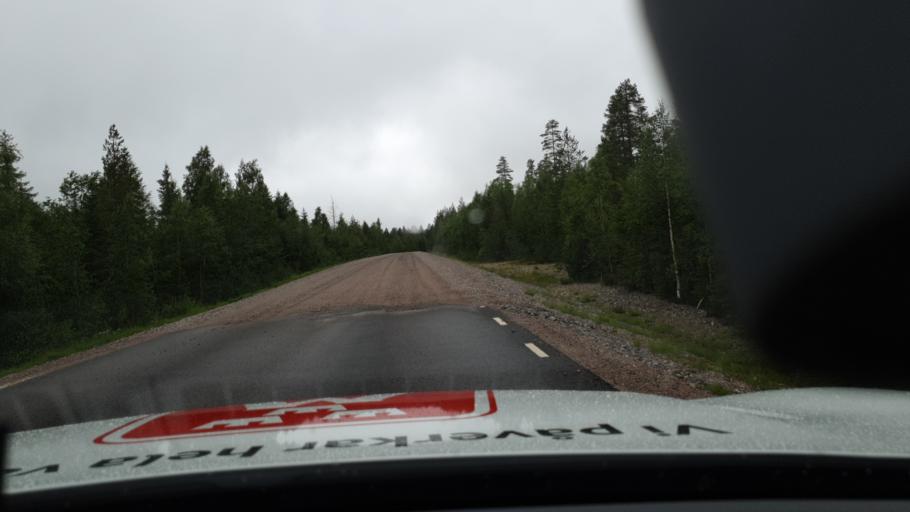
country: SE
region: Norrbotten
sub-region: Overtornea Kommun
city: OEvertornea
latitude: 66.4395
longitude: 23.5008
